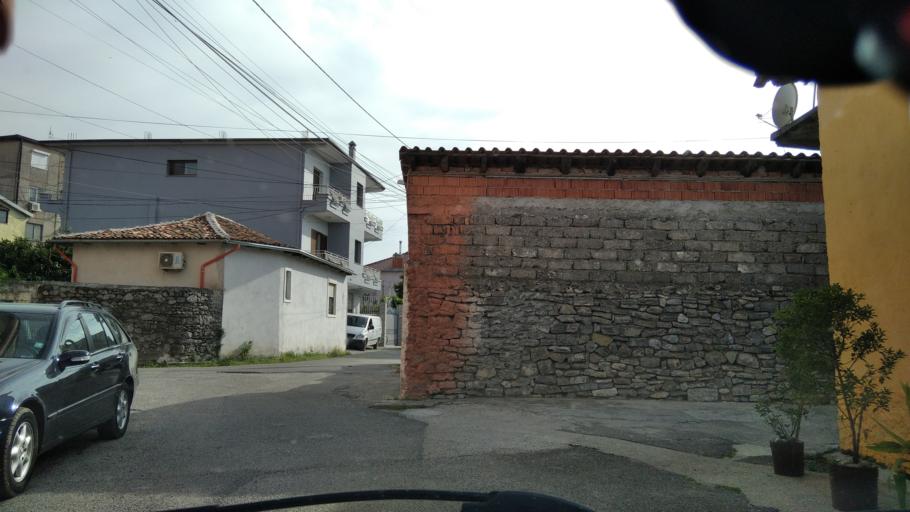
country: AL
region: Shkoder
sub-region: Rrethi i Shkodres
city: Shkoder
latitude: 42.0610
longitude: 19.5088
